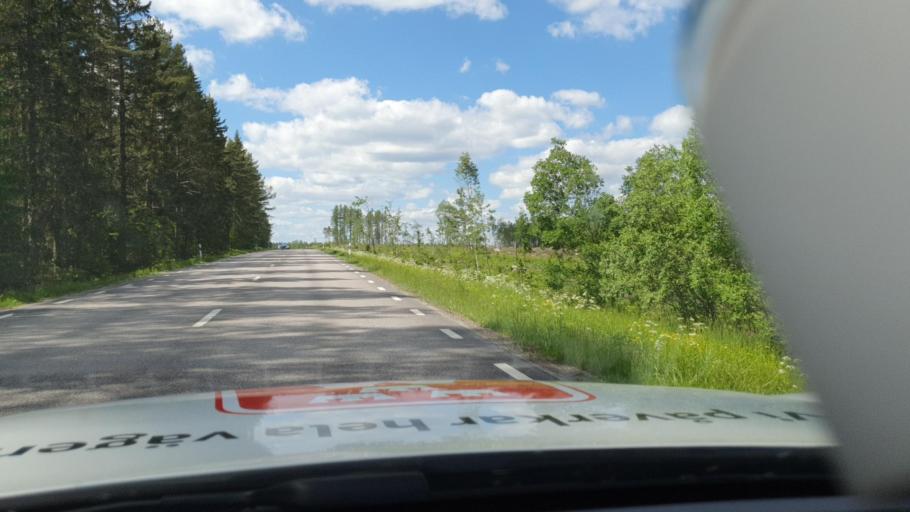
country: SE
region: Uppsala
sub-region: Tierps Kommun
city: Karlholmsbruk
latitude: 60.5435
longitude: 17.5419
